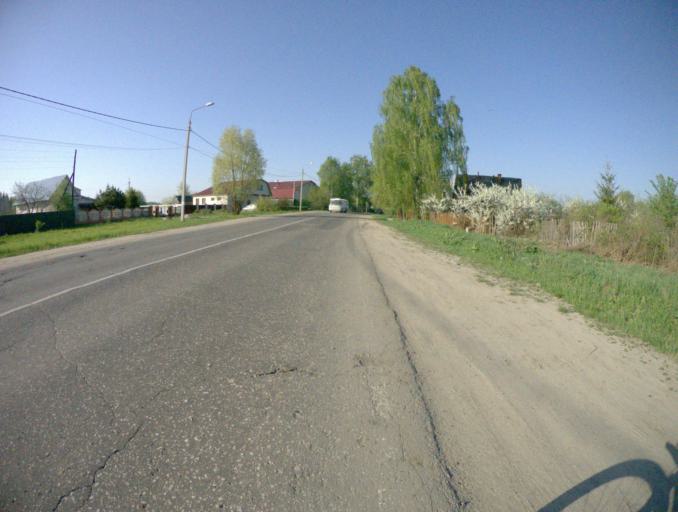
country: RU
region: Vladimir
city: Novovyazniki
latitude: 56.2161
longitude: 42.1815
